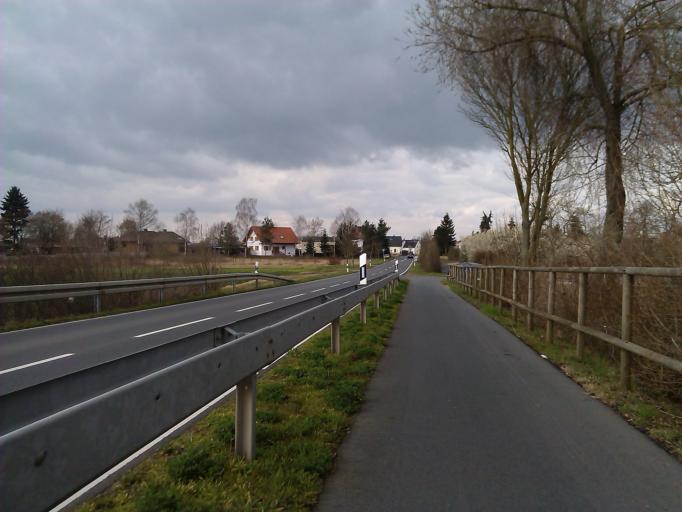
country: DE
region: Hesse
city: Pfungstadt
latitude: 49.8067
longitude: 8.5707
